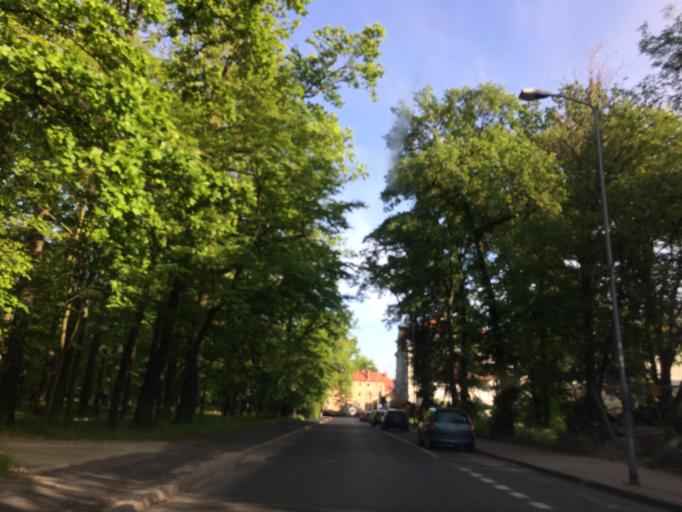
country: PL
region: Lower Silesian Voivodeship
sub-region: Powiat swidnicki
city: Swidnica
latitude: 50.8374
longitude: 16.4835
